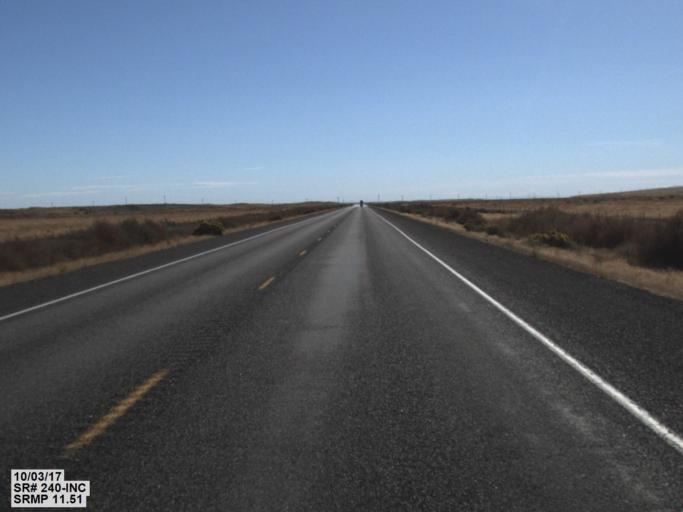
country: US
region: Washington
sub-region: Benton County
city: Benton City
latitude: 46.4733
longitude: -119.5548
